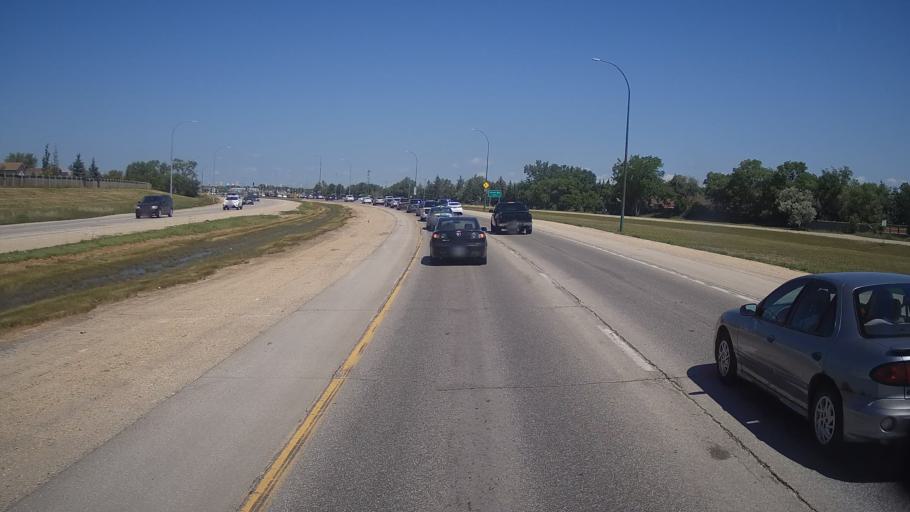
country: CA
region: Manitoba
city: Winnipeg
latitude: 49.9190
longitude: -97.0489
